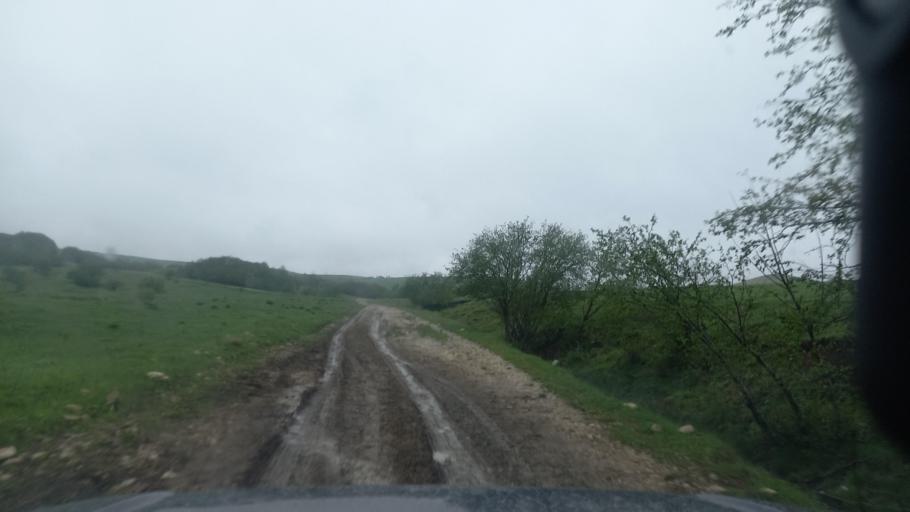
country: RU
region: Kabardino-Balkariya
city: Kamennomostskoye
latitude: 43.6923
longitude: 42.9986
